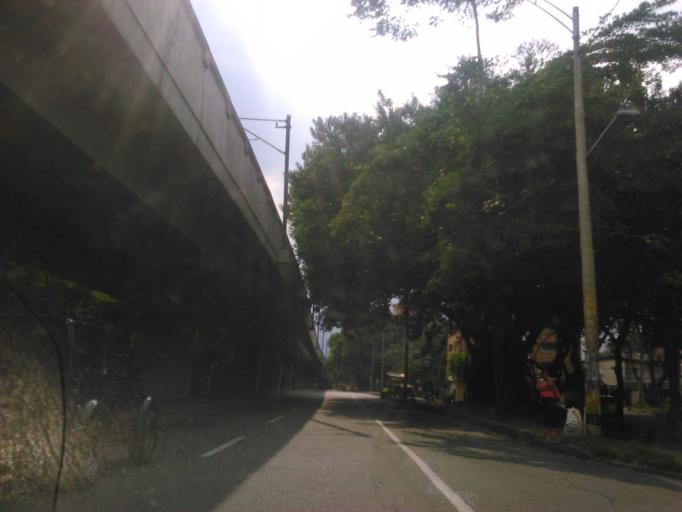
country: CO
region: Antioquia
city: Medellin
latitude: 6.2581
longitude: -75.5943
